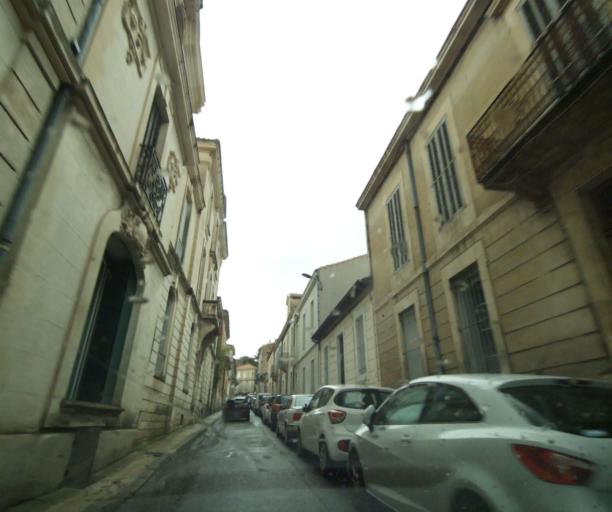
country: FR
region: Languedoc-Roussillon
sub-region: Departement du Gard
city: Nimes
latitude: 43.8427
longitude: 4.3552
